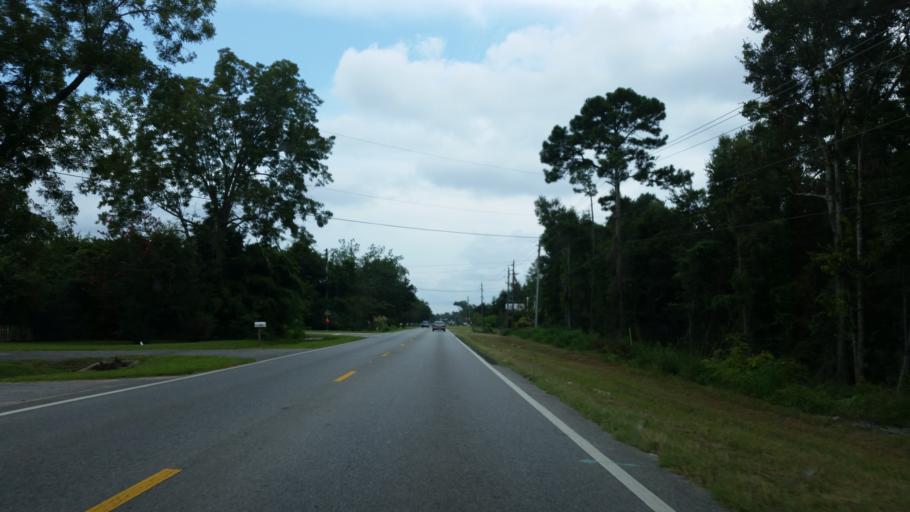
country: US
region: Florida
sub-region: Santa Rosa County
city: Pace
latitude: 30.6088
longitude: -87.1614
